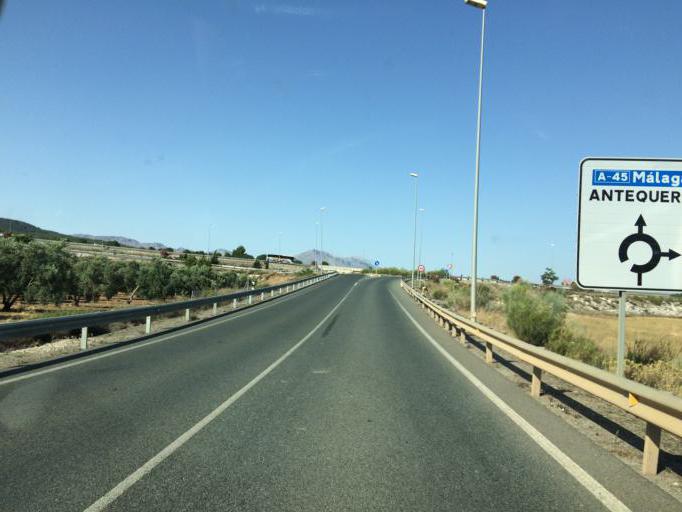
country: ES
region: Andalusia
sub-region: Provincia de Malaga
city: Antequera
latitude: 37.0467
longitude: -4.5081
